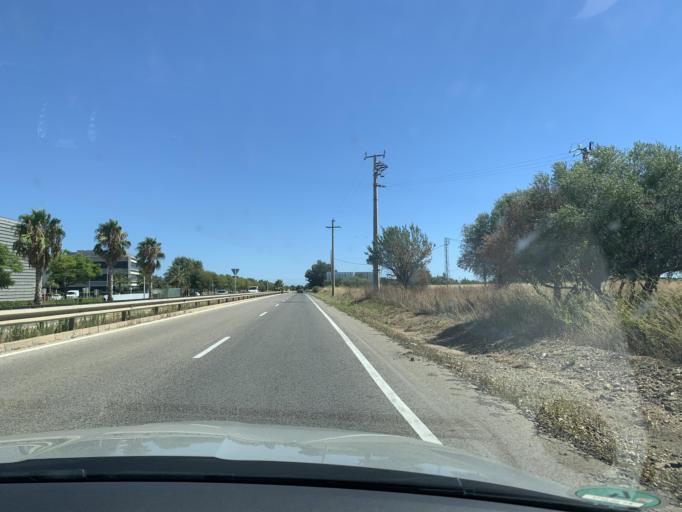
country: ES
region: Catalonia
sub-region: Provincia de Tarragona
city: Reus
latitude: 41.1424
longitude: 1.1283
